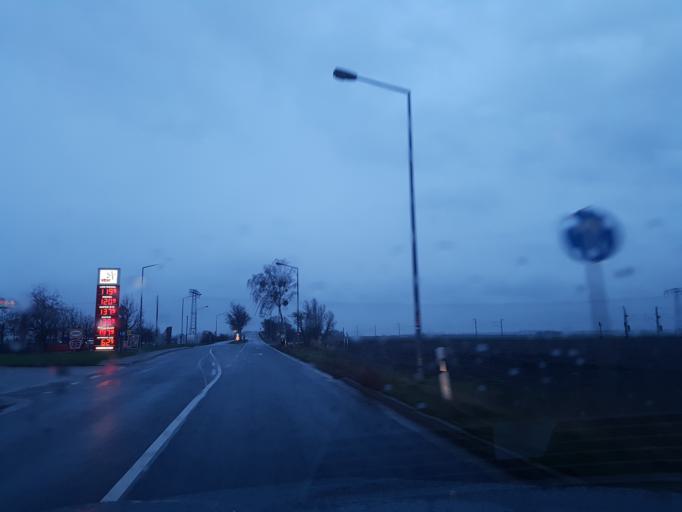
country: DE
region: Saxony
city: Grossenhain
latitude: 51.2797
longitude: 13.5209
